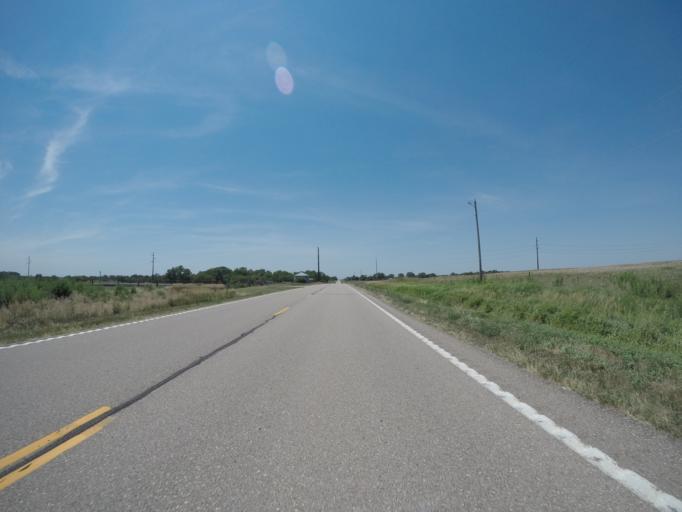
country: US
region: Kansas
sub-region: Dickinson County
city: Solomon
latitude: 39.0307
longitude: -97.5302
